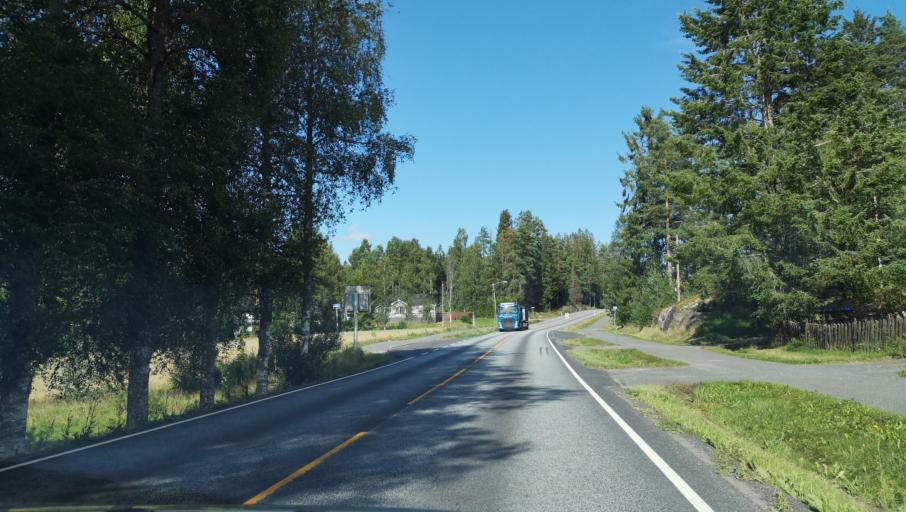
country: NO
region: Ostfold
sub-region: Valer
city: Kirkebygda
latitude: 59.5667
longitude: 10.8567
